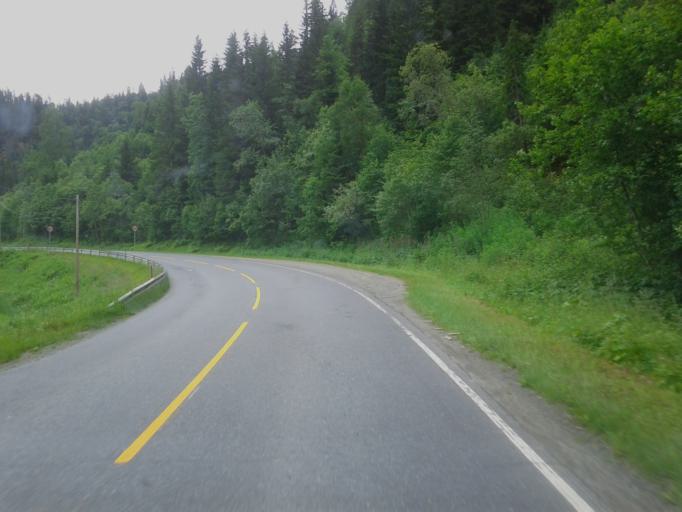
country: NO
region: Sor-Trondelag
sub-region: Midtre Gauldal
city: Storen
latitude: 62.9939
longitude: 10.4708
